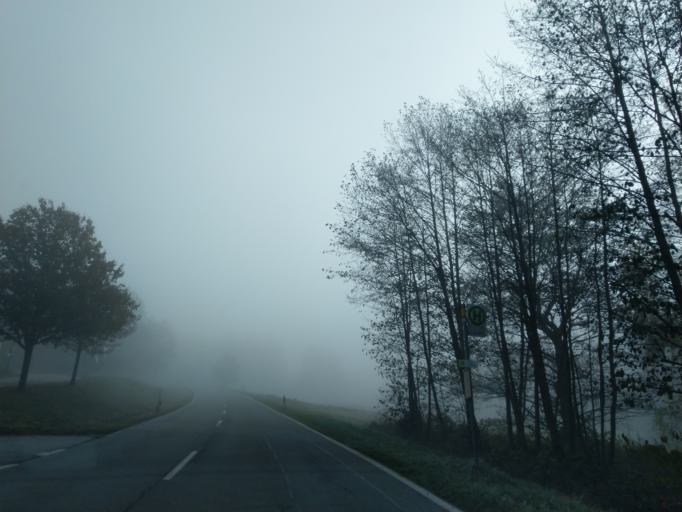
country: DE
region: Bavaria
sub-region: Lower Bavaria
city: Aussernzell
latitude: 48.7241
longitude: 13.2155
